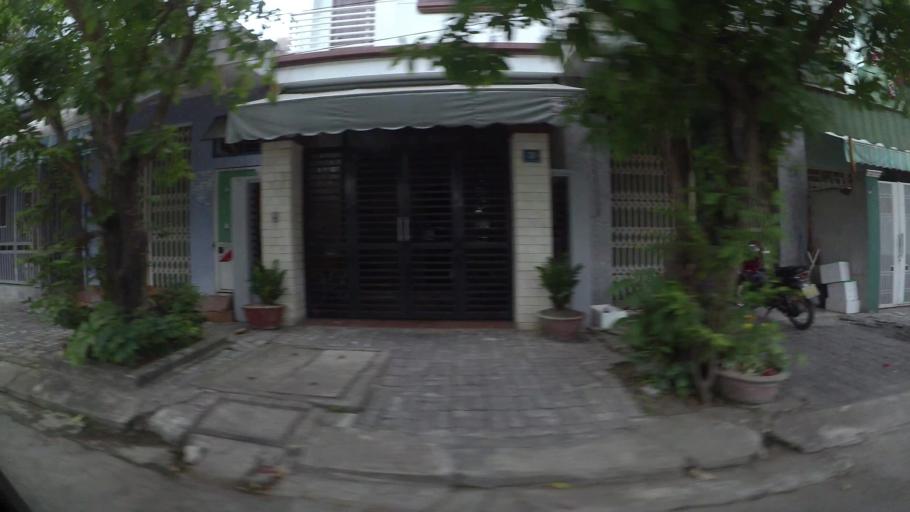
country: VN
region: Da Nang
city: Thanh Khe
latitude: 16.0622
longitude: 108.1834
